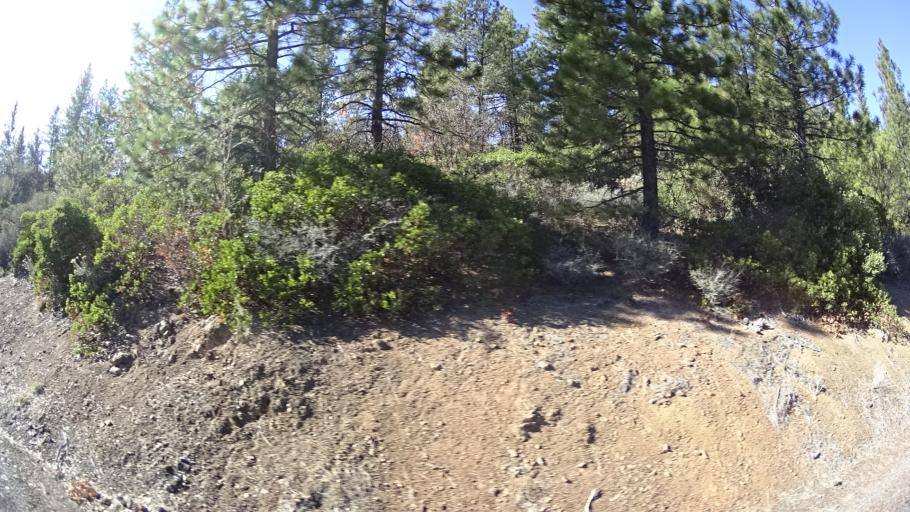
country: US
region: California
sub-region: Siskiyou County
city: Weed
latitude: 41.4281
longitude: -122.6369
